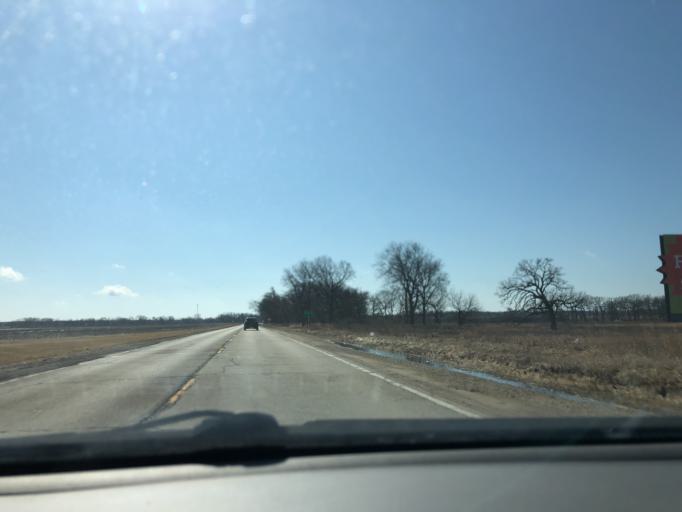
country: US
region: Illinois
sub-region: Kane County
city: Pingree Grove
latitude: 42.1000
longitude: -88.4546
